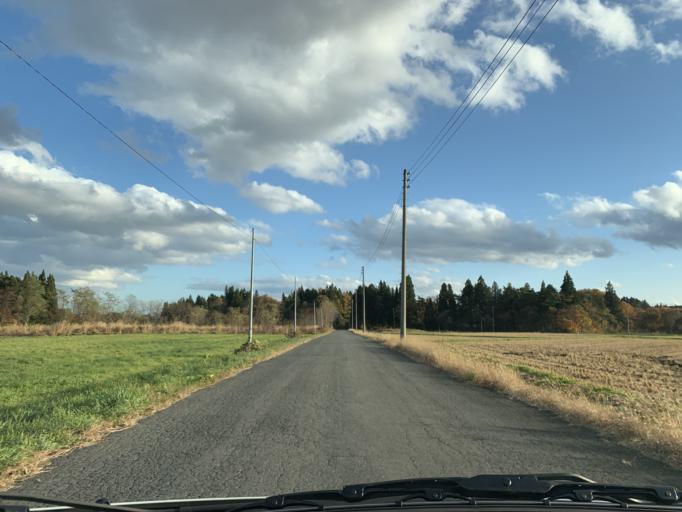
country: JP
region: Iwate
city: Mizusawa
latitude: 39.1182
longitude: 140.9976
